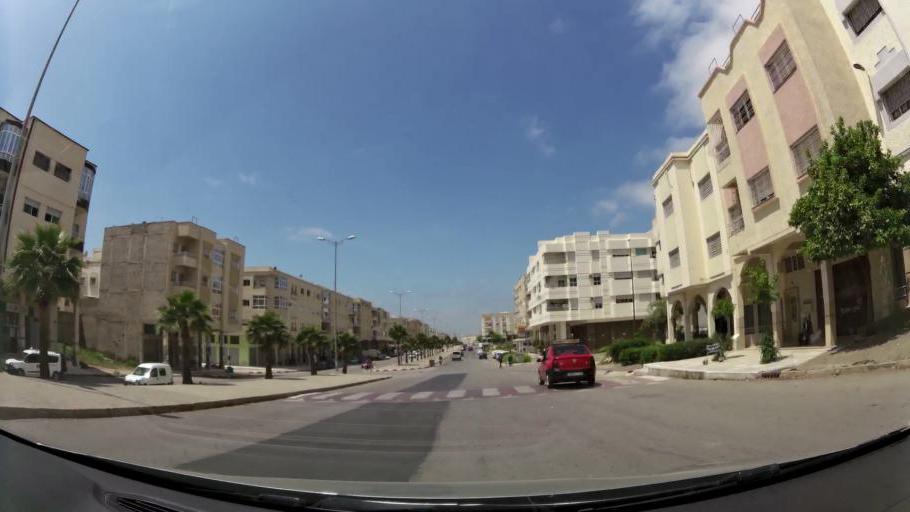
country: MA
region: Fes-Boulemane
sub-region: Fes
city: Fes
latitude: 34.0608
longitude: -5.0197
